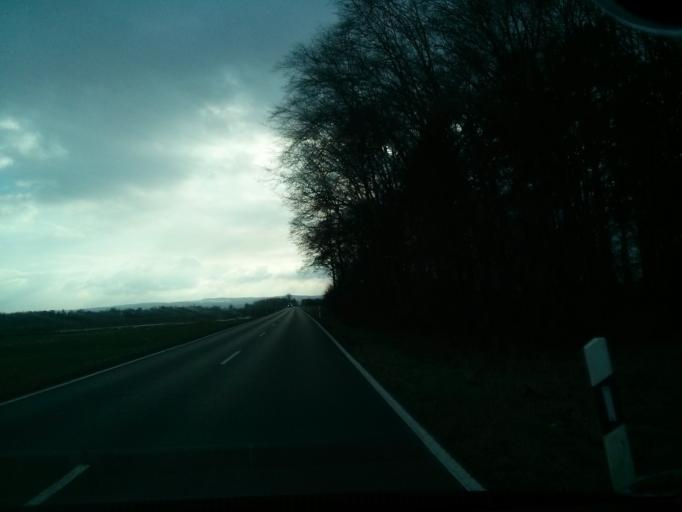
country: DE
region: North Rhine-Westphalia
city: Meckenheim
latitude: 50.6611
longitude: 7.0065
